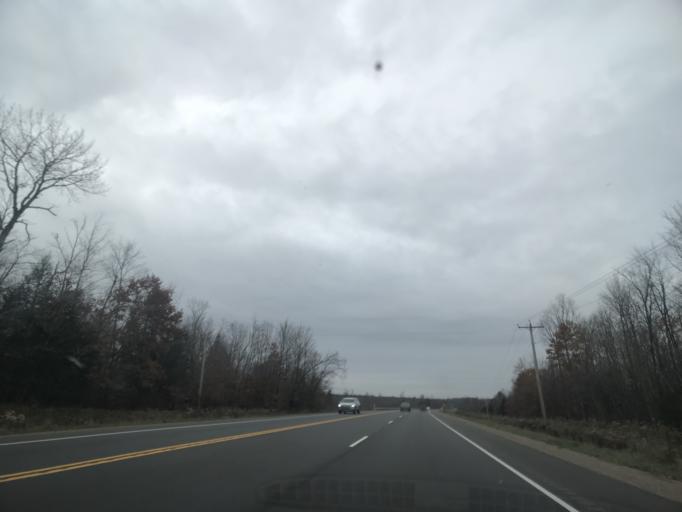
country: US
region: Wisconsin
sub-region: Menominee County
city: Legend Lake
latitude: 45.2278
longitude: -88.5160
